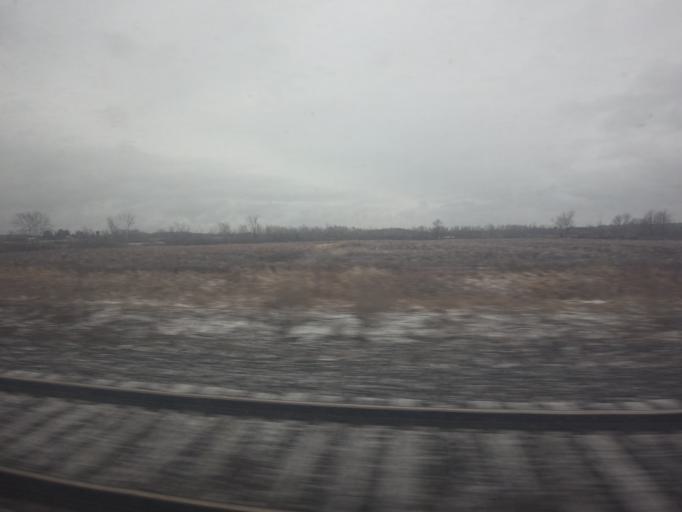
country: CA
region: Ontario
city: Gananoque
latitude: 44.3735
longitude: -76.1104
